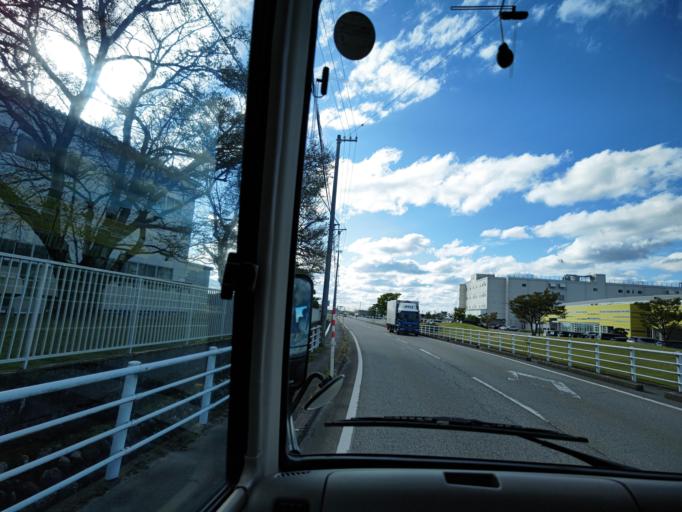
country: JP
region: Toyama
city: Nyuzen
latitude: 36.8933
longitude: 137.4361
